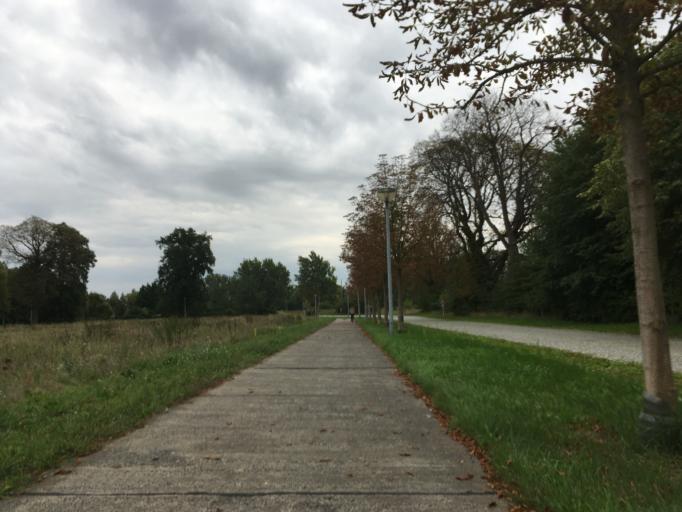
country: DE
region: Brandenburg
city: Schwedt (Oder)
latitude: 53.0678
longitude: 14.2758
